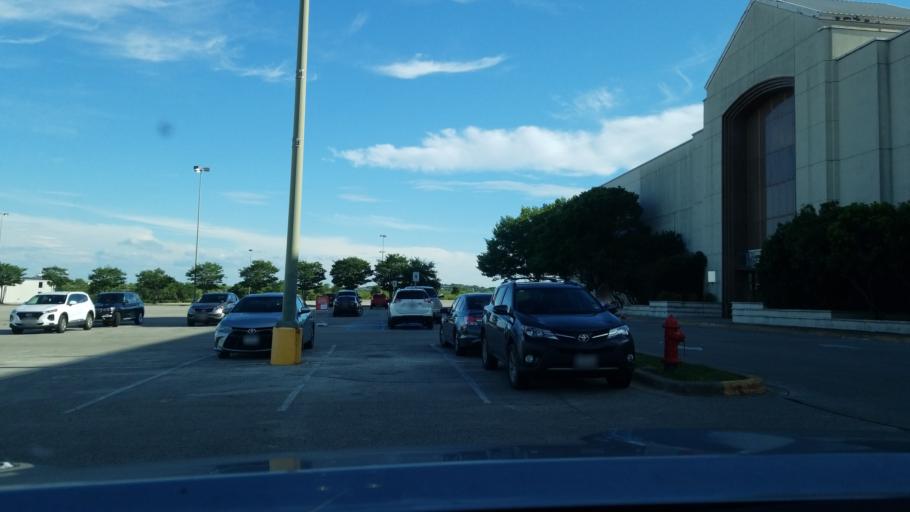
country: US
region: Texas
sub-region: Bexar County
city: Live Oak
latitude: 29.5972
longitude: -98.3480
